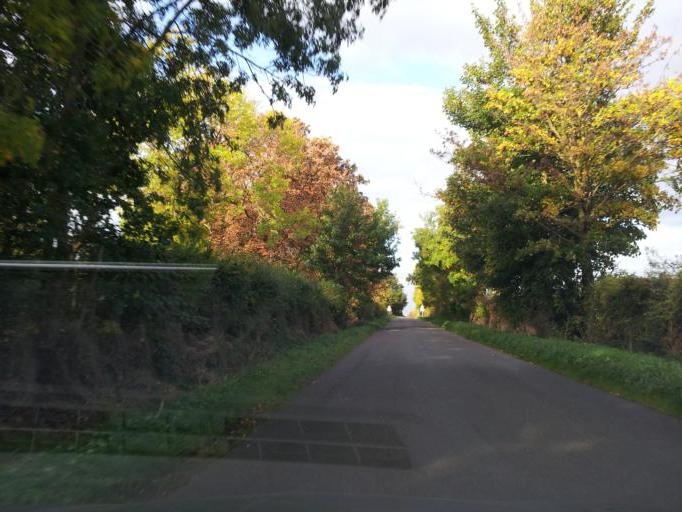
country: GB
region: England
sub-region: Lincolnshire
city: Long Bennington
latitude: 52.9840
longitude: -0.7968
